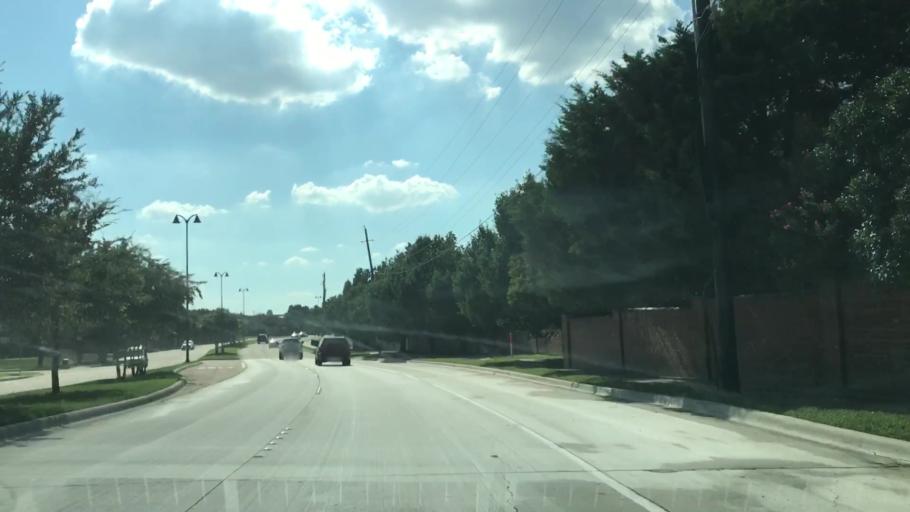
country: US
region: Texas
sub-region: Tarrant County
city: Keller
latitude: 32.9001
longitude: -97.2337
